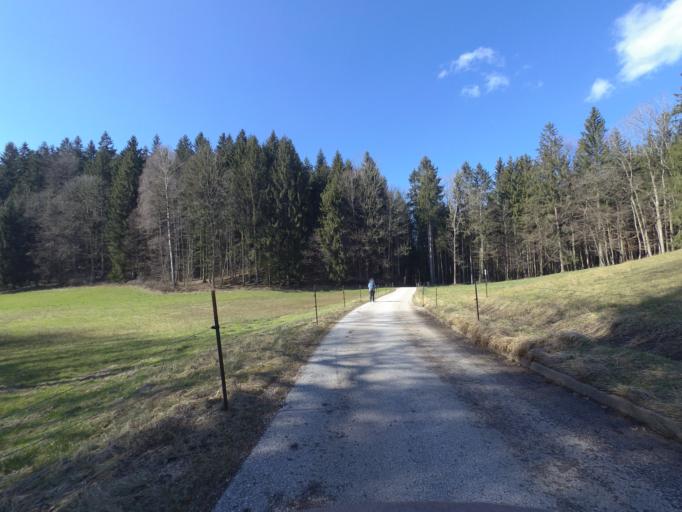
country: DE
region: Bavaria
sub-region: Upper Bavaria
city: Piding
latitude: 47.7850
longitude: 12.9155
